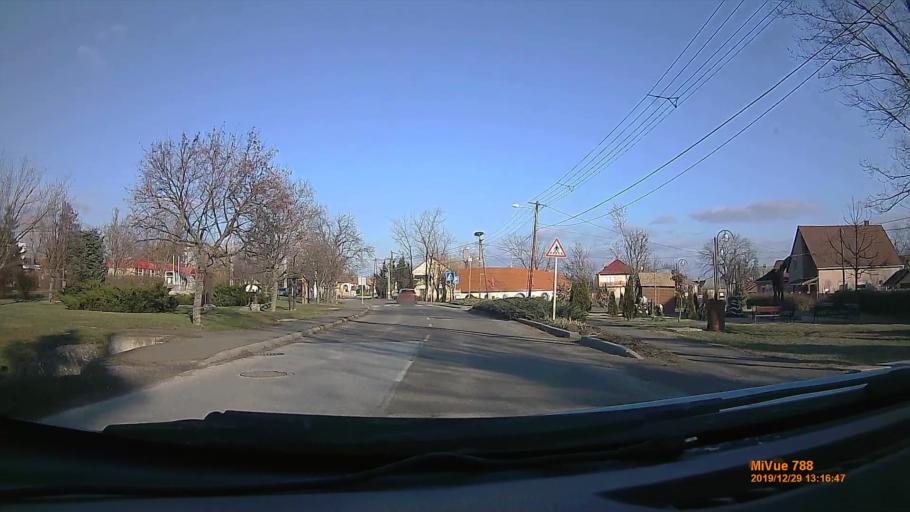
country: HU
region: Heves
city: Domoszlo
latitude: 47.8273
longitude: 20.1182
